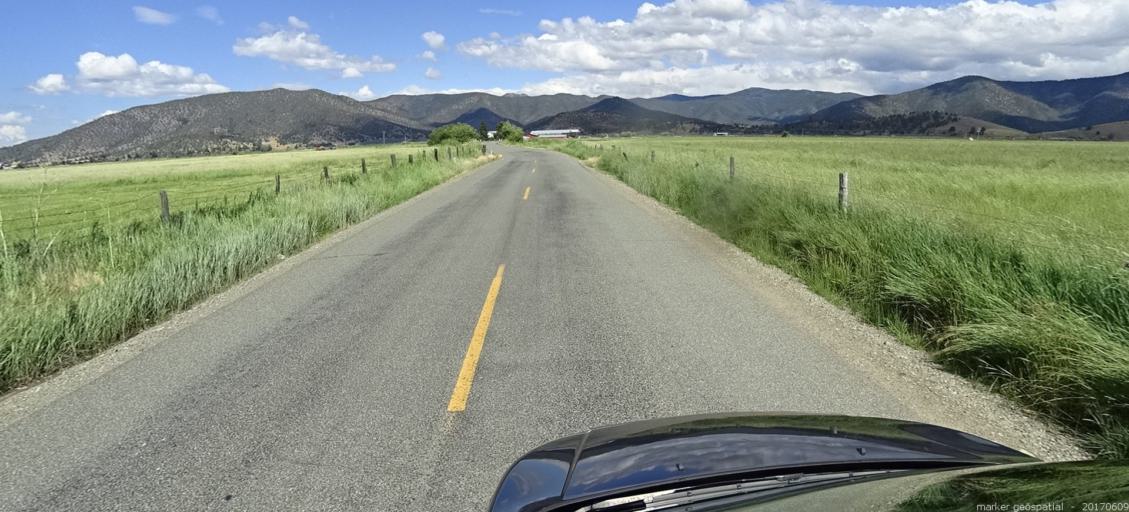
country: US
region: California
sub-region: Siskiyou County
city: Yreka
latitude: 41.4897
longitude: -122.8641
